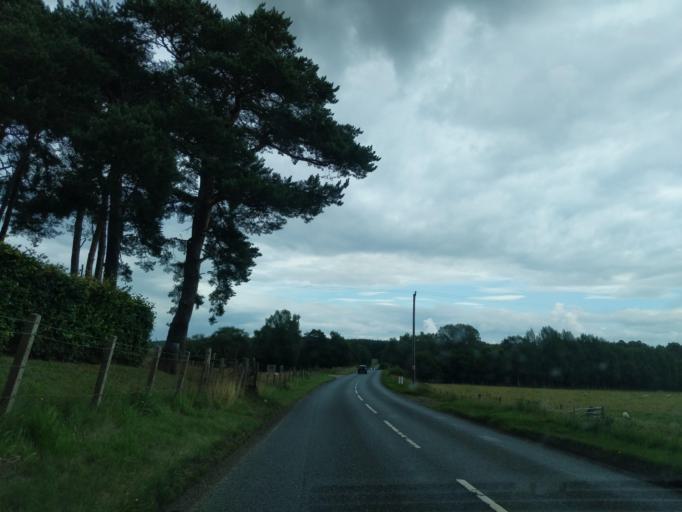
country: GB
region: Scotland
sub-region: Highland
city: Aviemore
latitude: 57.2963
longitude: -3.7861
